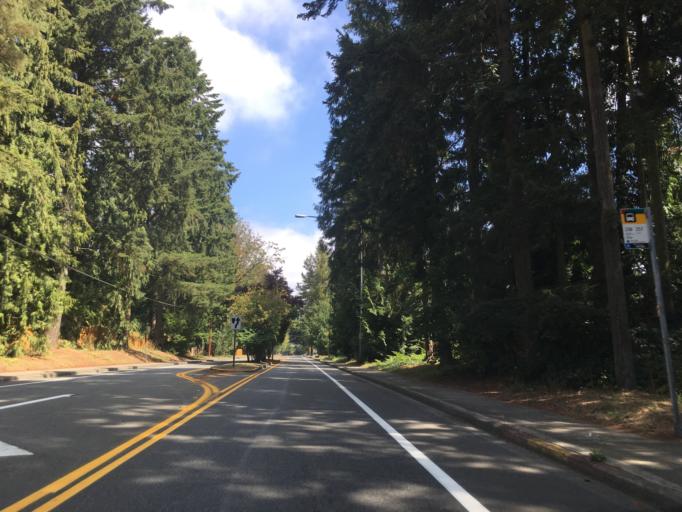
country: US
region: Washington
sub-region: King County
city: Kingsgate
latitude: 47.7279
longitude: -122.2000
